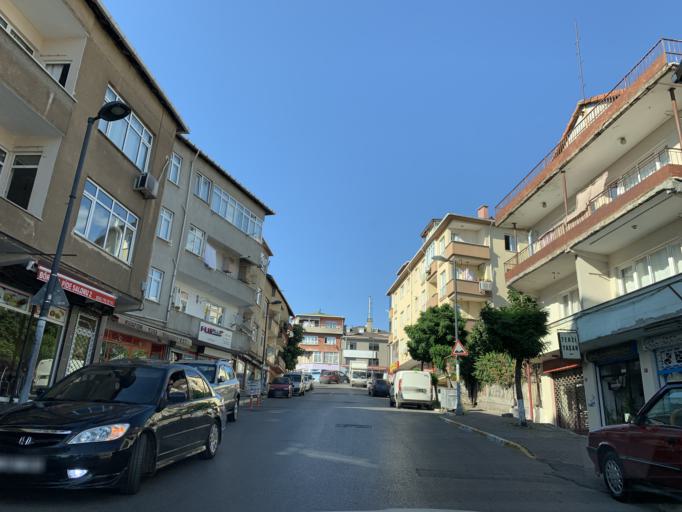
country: TR
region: Istanbul
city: Pendik
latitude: 40.8897
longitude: 29.2448
